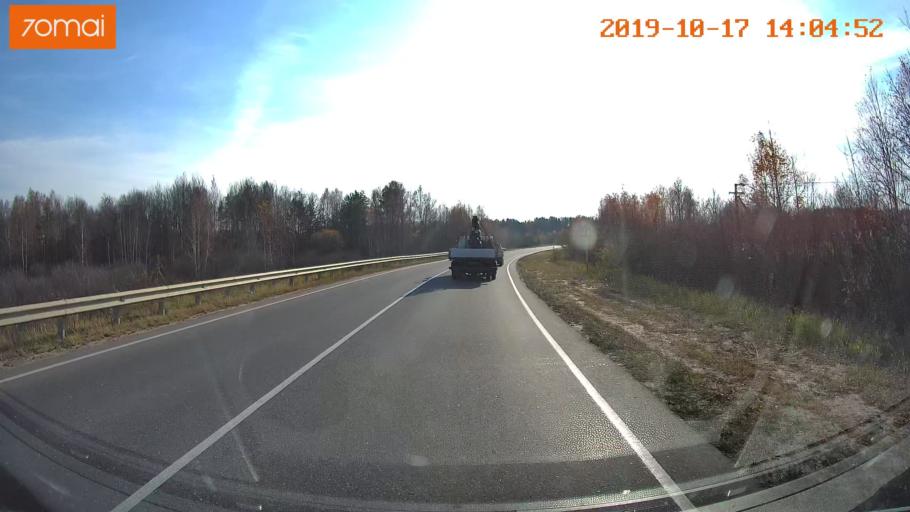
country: RU
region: Rjazan
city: Spas-Klepiki
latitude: 55.1214
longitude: 40.1331
